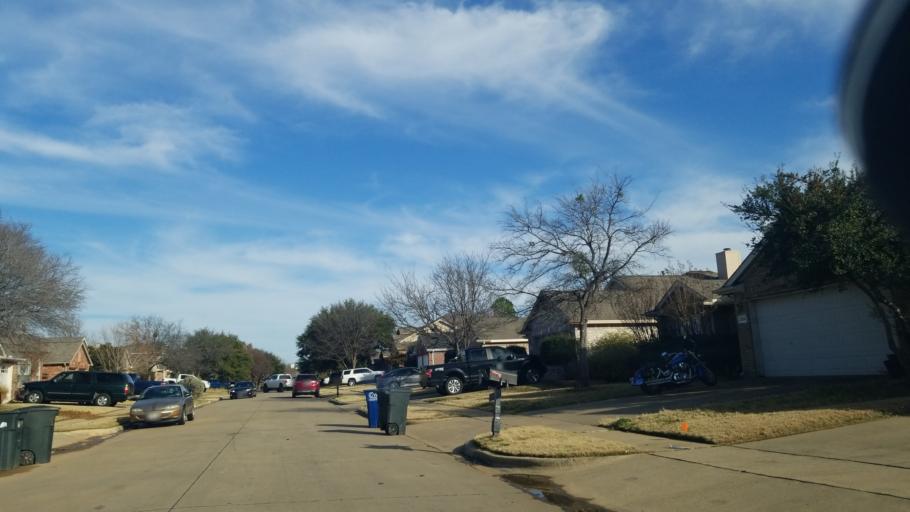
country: US
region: Texas
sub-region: Denton County
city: Corinth
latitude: 33.1411
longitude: -97.0613
